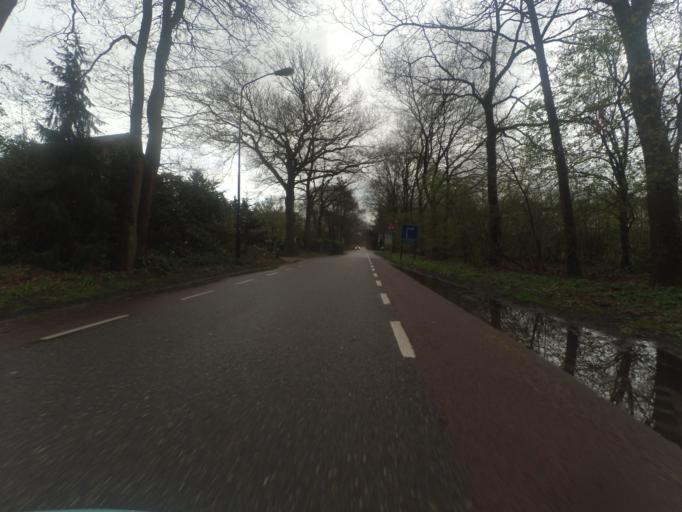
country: NL
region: Gelderland
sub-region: Gemeente Apeldoorn
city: Beekbergen
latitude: 52.1199
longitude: 5.8950
